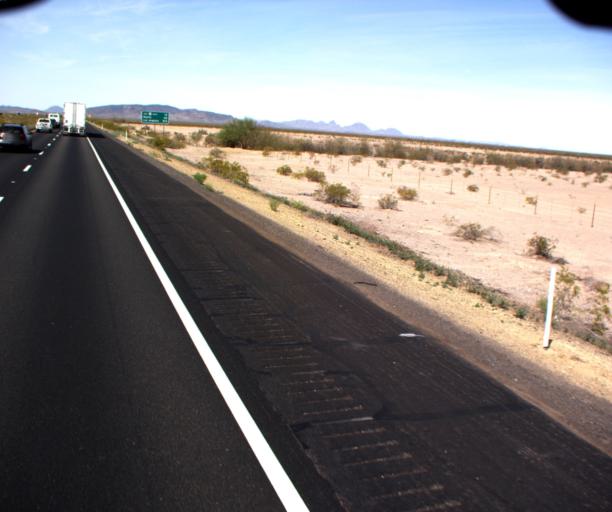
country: US
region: Arizona
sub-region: La Paz County
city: Salome
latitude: 33.6340
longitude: -113.7858
